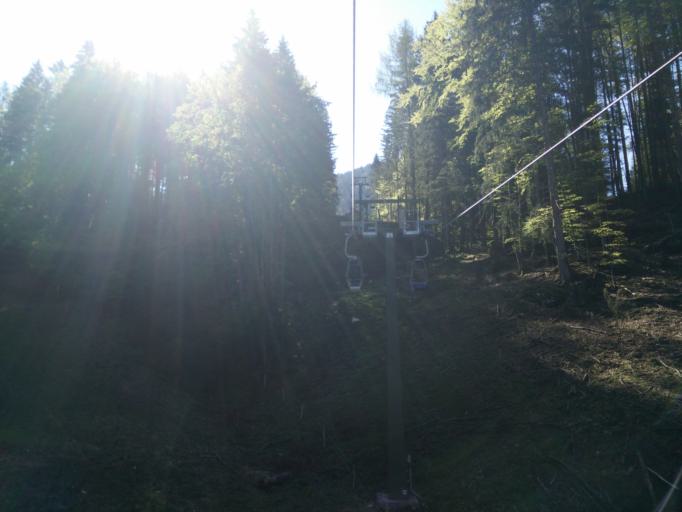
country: DE
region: Bavaria
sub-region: Upper Bavaria
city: Kiefersfelden
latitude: 47.5848
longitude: 12.1967
